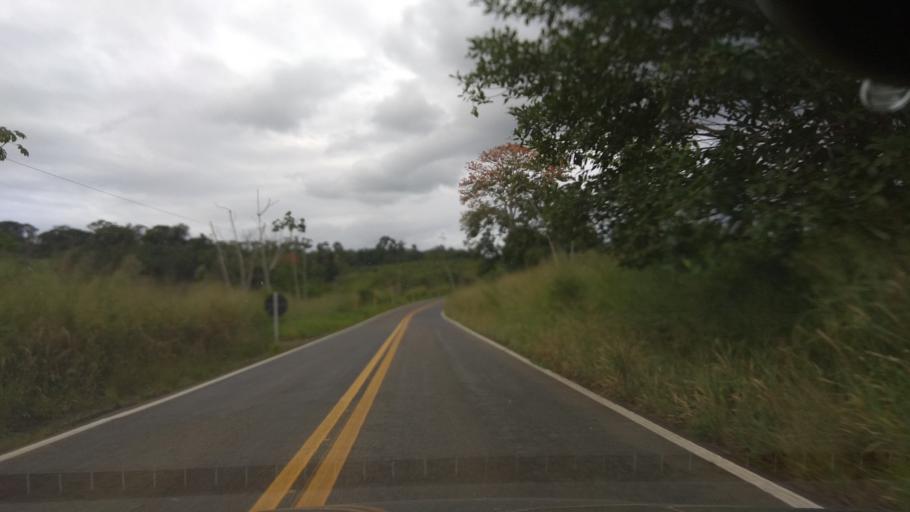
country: BR
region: Bahia
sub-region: Ubata
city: Ubata
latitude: -14.2043
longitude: -39.5742
